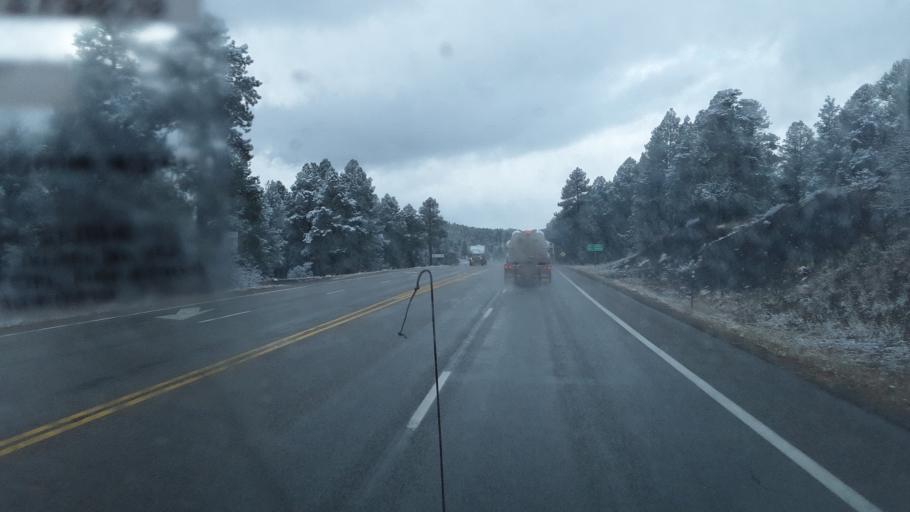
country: US
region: Colorado
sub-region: Archuleta County
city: Pagosa Springs
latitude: 37.2097
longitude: -107.2596
